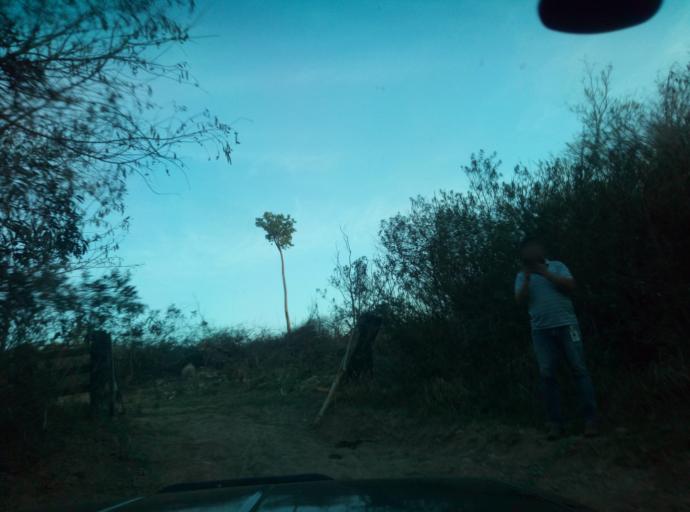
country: PY
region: Caaguazu
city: Yhu
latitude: -25.1989
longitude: -56.1106
